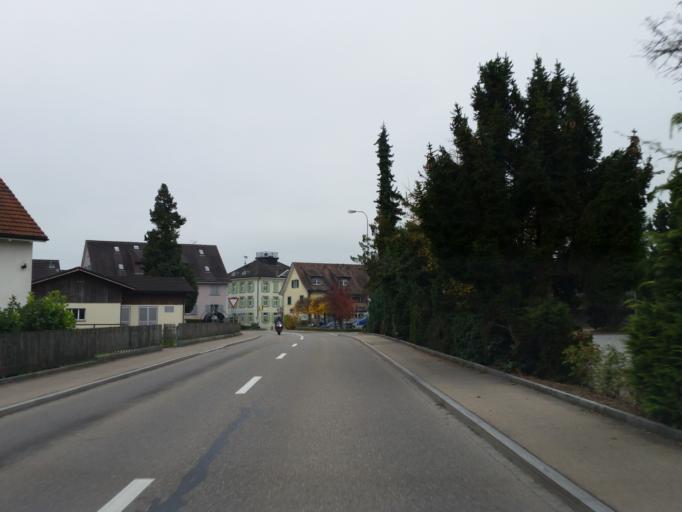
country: CH
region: Thurgau
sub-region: Arbon District
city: Uttwil
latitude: 47.5770
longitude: 9.3194
